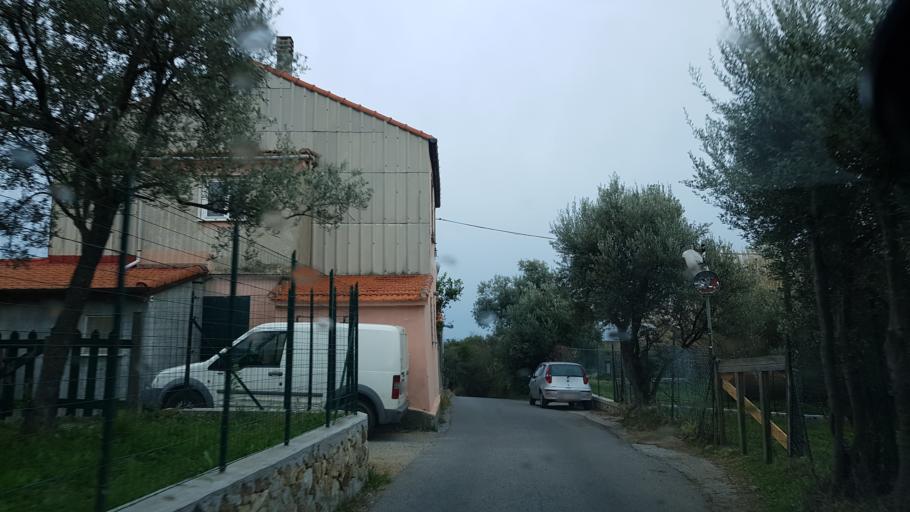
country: IT
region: Liguria
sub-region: Provincia di Savona
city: Valleggia
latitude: 44.3047
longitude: 8.4467
